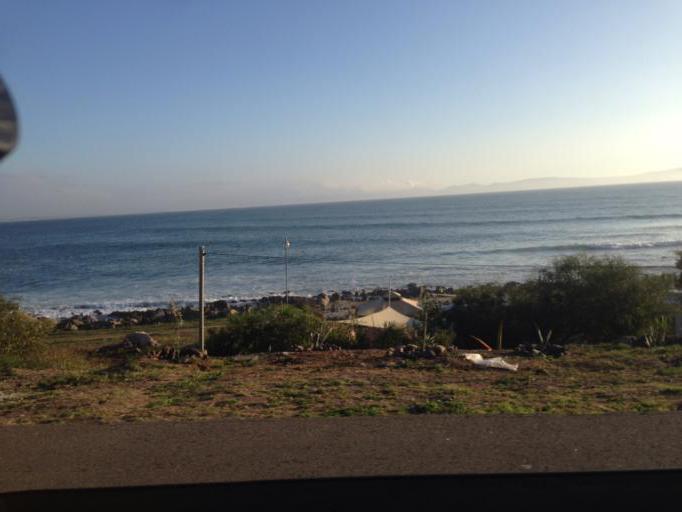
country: MX
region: Baja California
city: Ensenada
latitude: 31.8613
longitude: -116.6457
